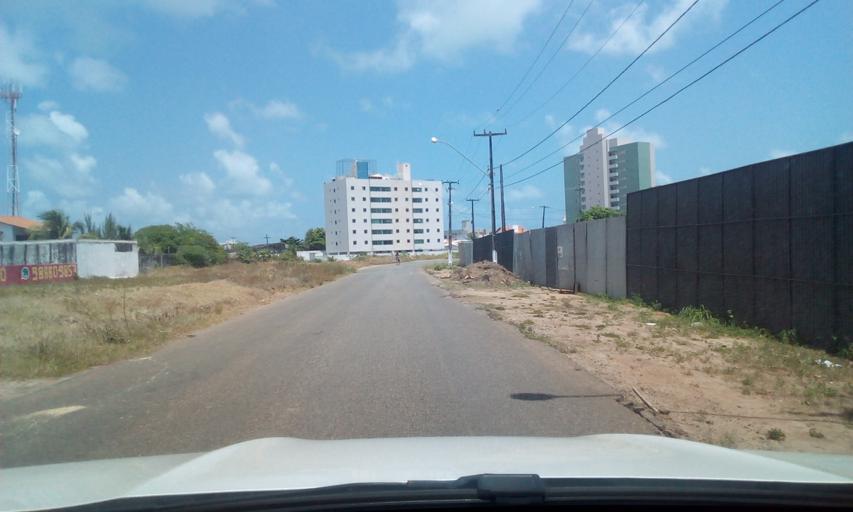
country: BR
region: Paraiba
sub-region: Cabedelo
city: Cabedelo
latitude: -7.0310
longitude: -34.8374
